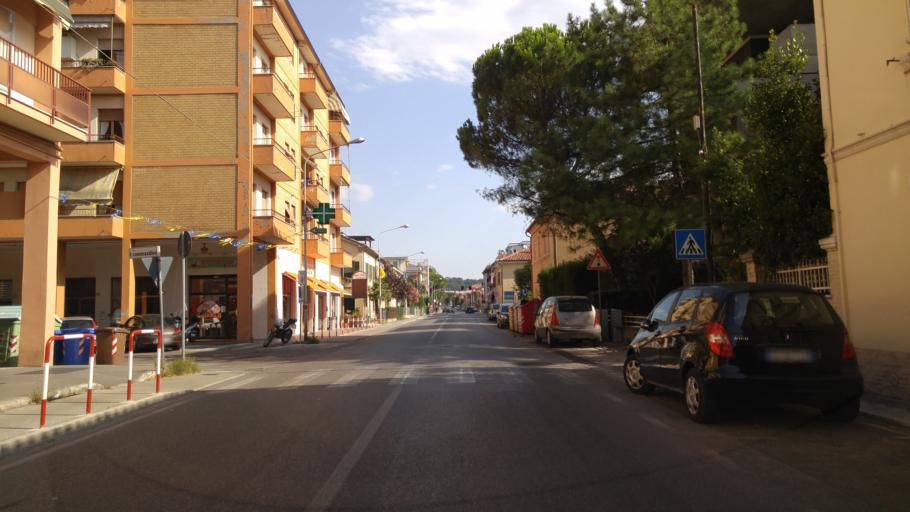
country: IT
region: The Marches
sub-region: Provincia di Pesaro e Urbino
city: Pesaro
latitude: 43.8986
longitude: 12.9204
